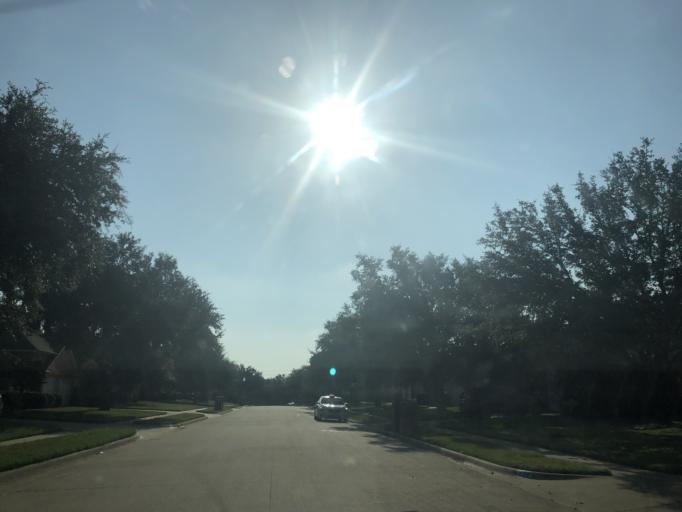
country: US
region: Texas
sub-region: Tarrant County
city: Euless
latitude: 32.8705
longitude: -97.0849
